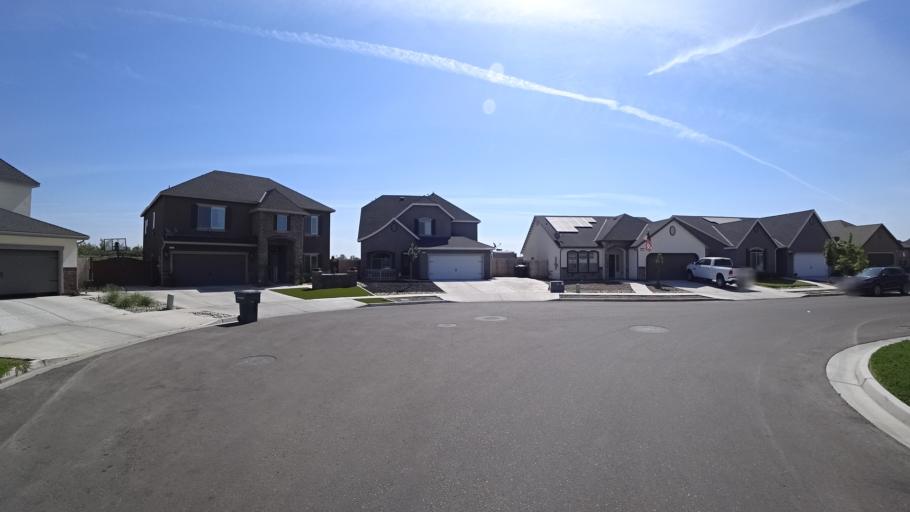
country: US
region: California
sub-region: Kings County
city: Hanford
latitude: 36.3387
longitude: -119.6794
